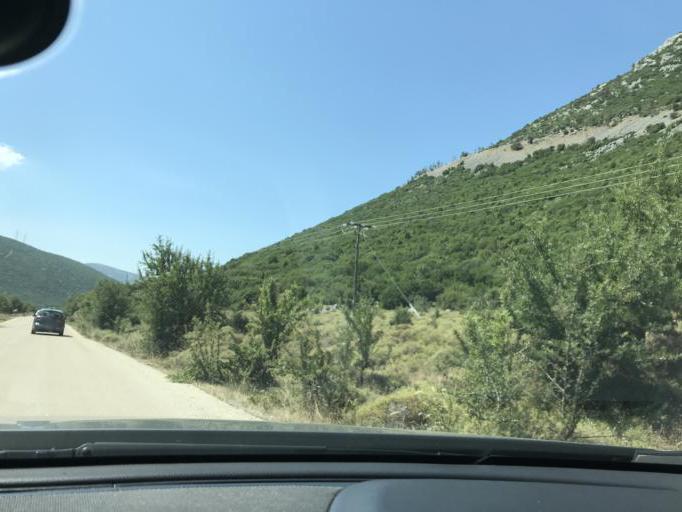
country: GR
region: Central Greece
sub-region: Nomos Voiotias
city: Distomo
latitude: 38.4738
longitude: 22.6813
